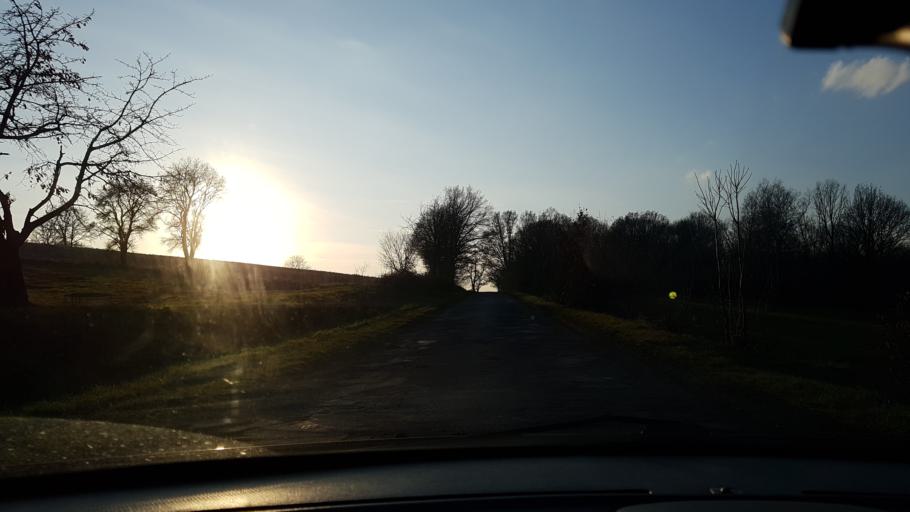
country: PL
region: Lower Silesian Voivodeship
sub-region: Powiat strzelinski
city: Przeworno
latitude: 50.6566
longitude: 17.0976
